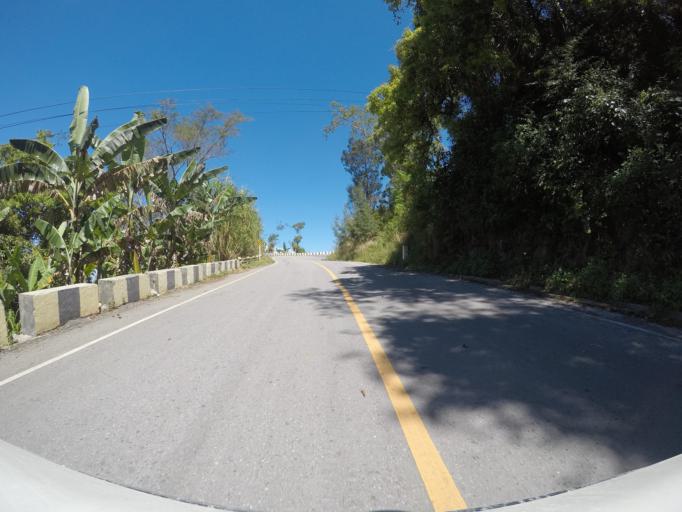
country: TL
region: Manatuto
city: Manatuto
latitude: -8.8049
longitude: 125.9697
